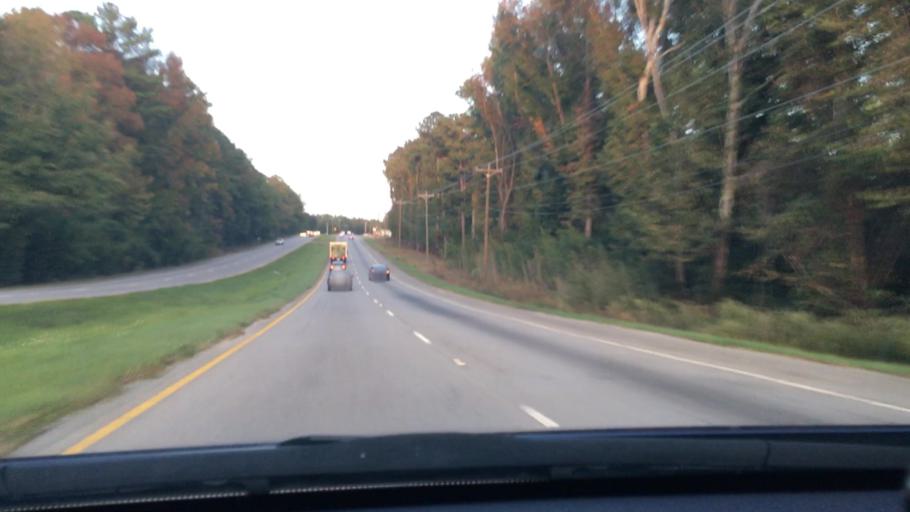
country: US
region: South Carolina
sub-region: Richland County
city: Gadsden
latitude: 33.9406
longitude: -80.7828
